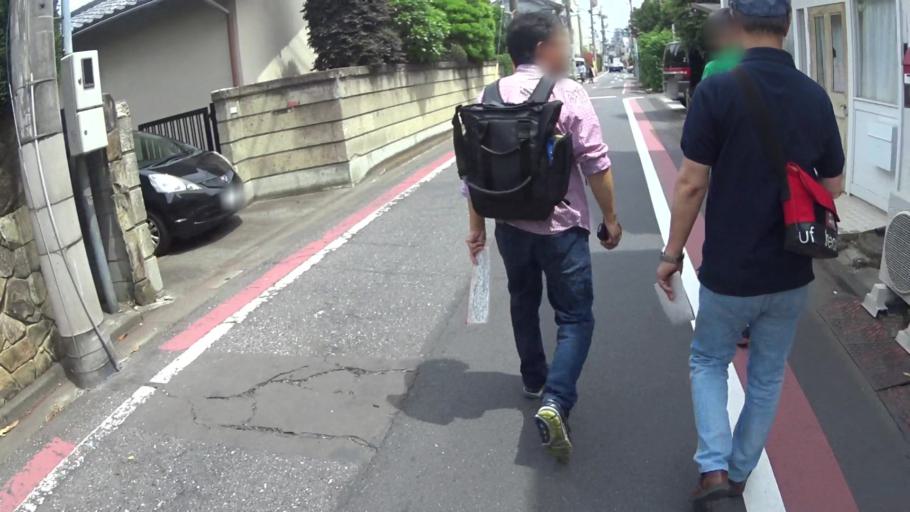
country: JP
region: Tokyo
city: Musashino
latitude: 35.7061
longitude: 139.5950
